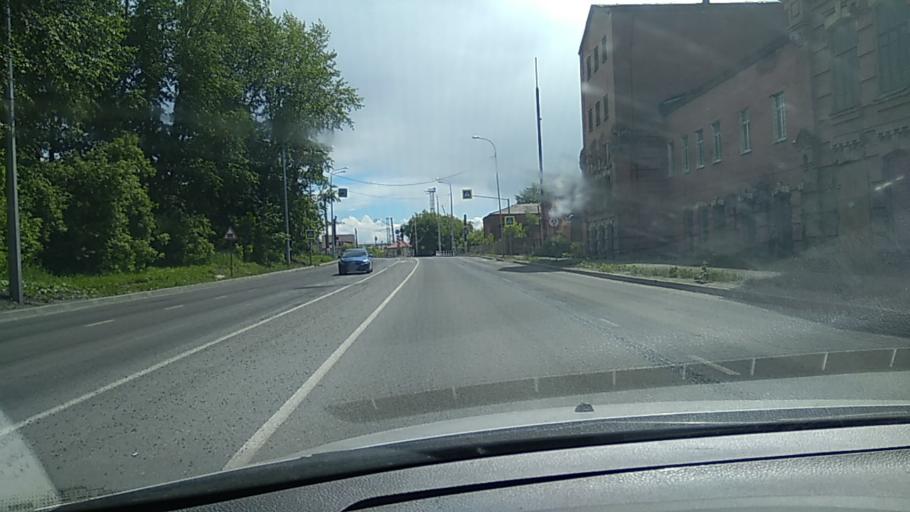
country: RU
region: Sverdlovsk
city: Nizhniy Tagil
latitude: 57.9149
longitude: 59.9905
